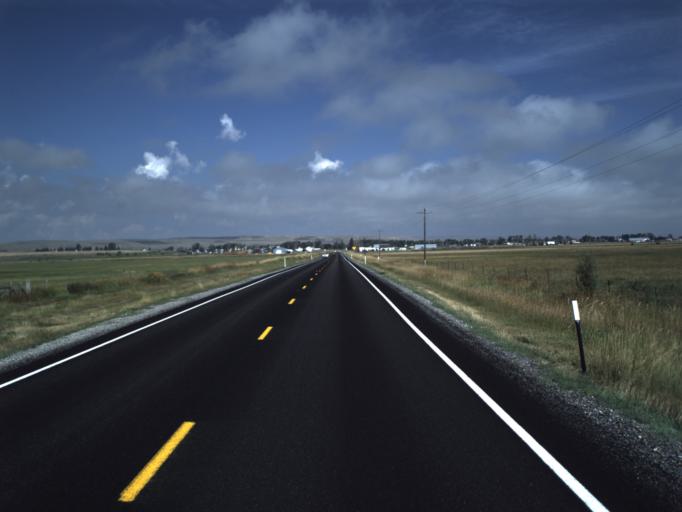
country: US
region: Utah
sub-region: Rich County
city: Randolph
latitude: 41.6450
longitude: -111.1836
